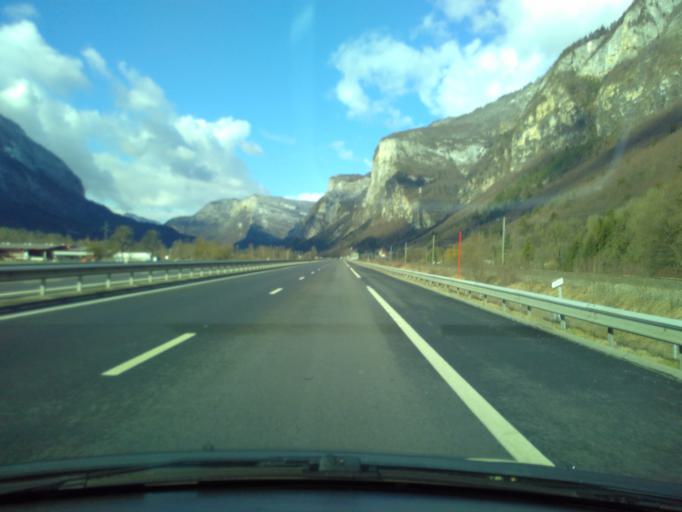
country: FR
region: Rhone-Alpes
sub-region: Departement de la Haute-Savoie
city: Magland
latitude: 45.9964
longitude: 6.6297
